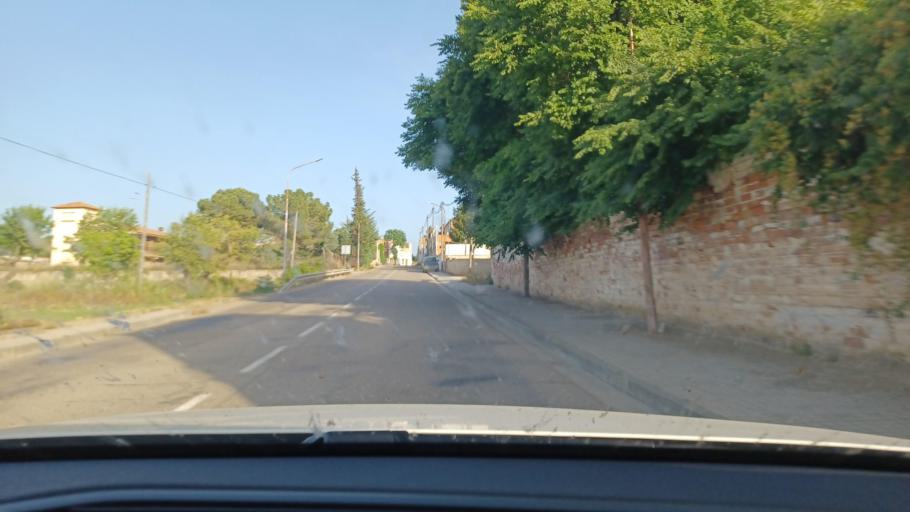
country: ES
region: Aragon
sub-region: Provincia de Zaragoza
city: Maella
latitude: 41.1184
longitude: 0.1440
